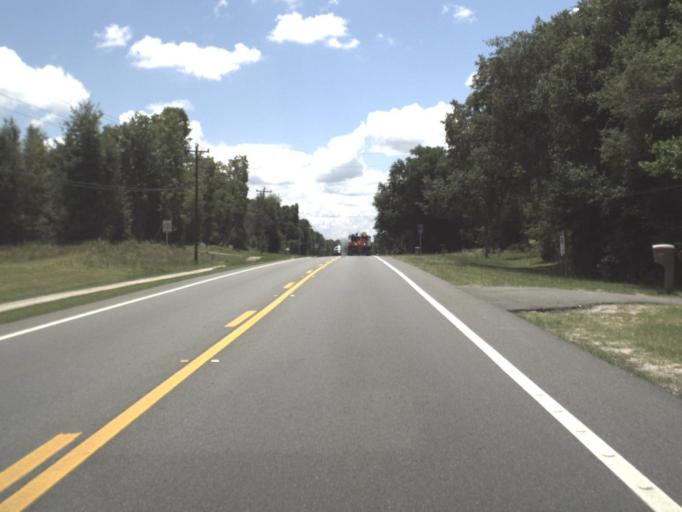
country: US
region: Florida
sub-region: Clay County
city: Keystone Heights
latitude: 29.7645
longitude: -82.0049
